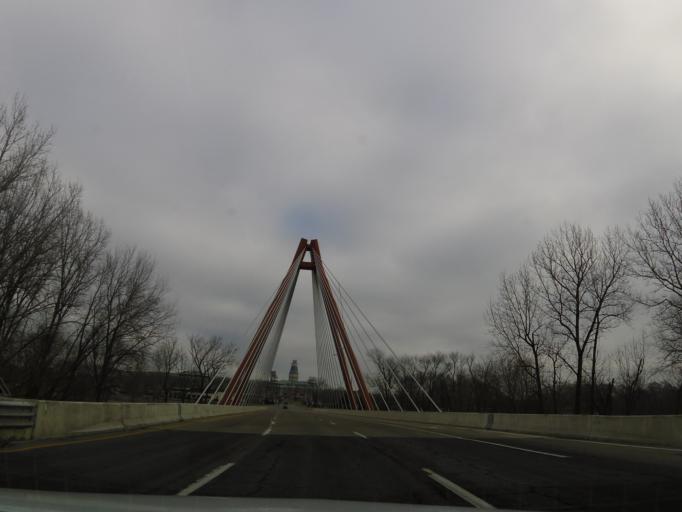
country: US
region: Indiana
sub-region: Bartholomew County
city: Columbus
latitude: 39.1977
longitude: -85.9259
